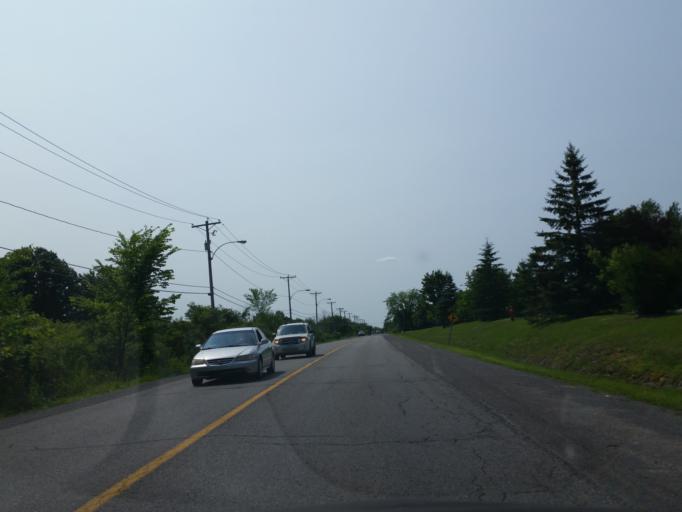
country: CA
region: Ontario
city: Bells Corners
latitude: 45.3851
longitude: -75.8245
